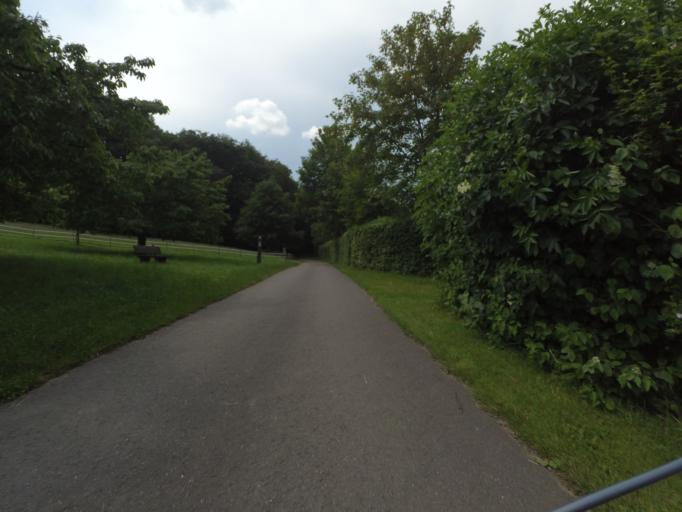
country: DE
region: Rheinland-Pfalz
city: Morshausen
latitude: 50.1916
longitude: 7.4372
